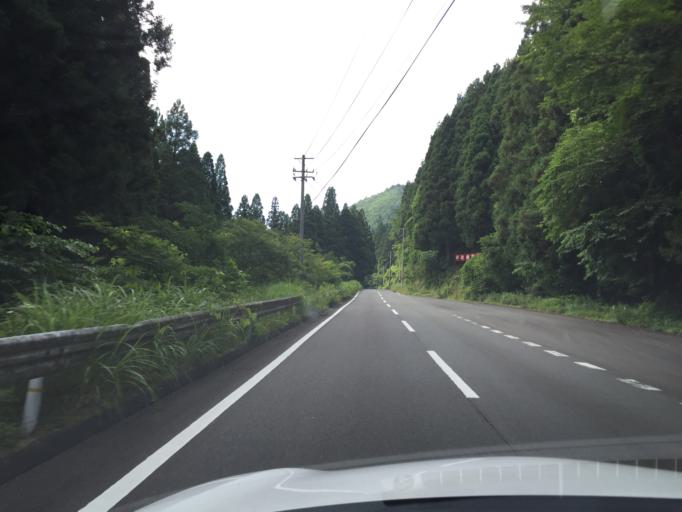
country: JP
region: Fukushima
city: Iwaki
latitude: 37.0719
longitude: 140.6886
